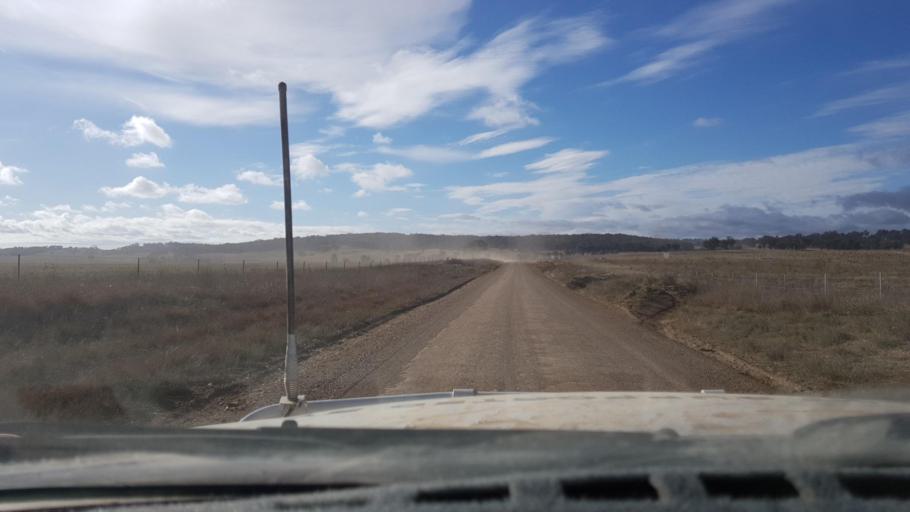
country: AU
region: New South Wales
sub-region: Armidale Dumaresq
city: Enmore
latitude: -30.7455
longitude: 151.6089
